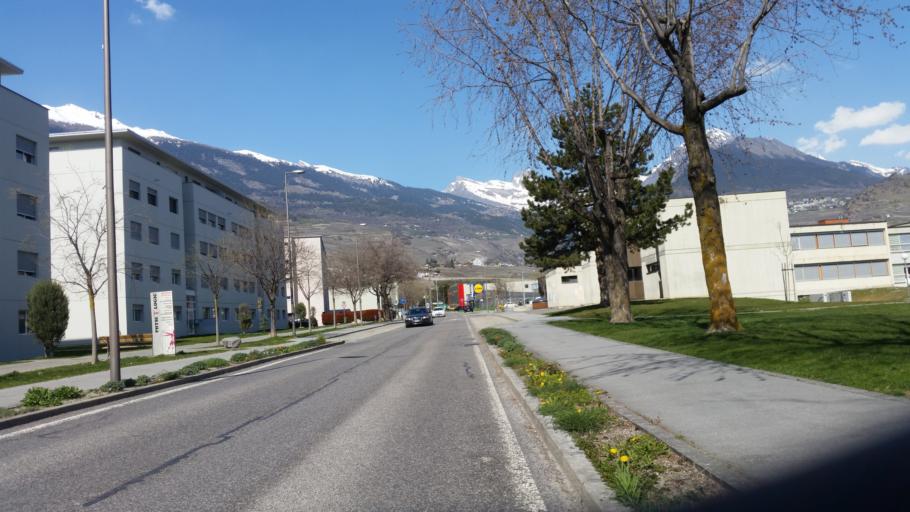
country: CH
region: Valais
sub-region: Conthey District
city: Conthey
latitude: 46.2212
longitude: 7.3036
